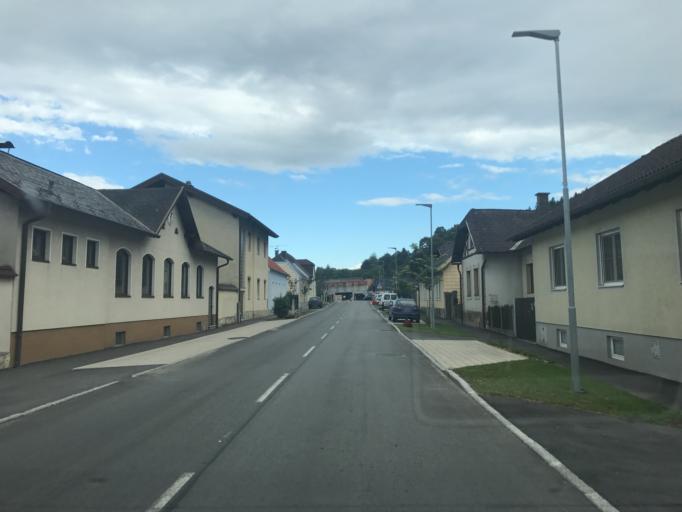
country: AT
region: Lower Austria
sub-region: Politischer Bezirk Wiener Neustadt
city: Markt Piesting
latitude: 47.8658
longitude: 16.1649
